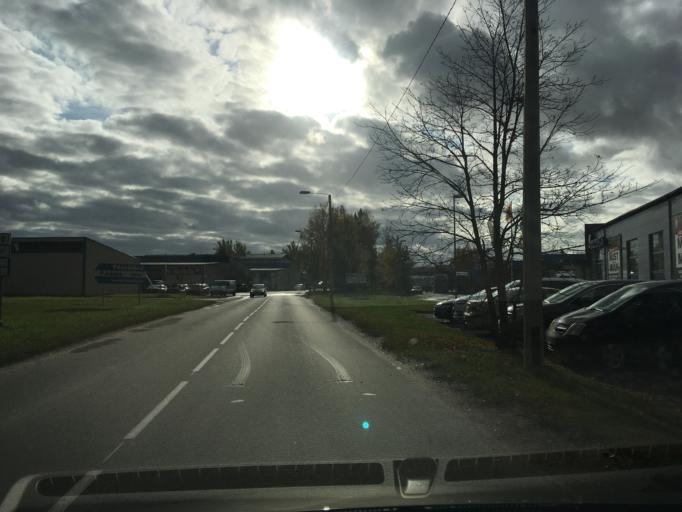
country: EE
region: Paernumaa
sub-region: Paernu linn
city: Parnu
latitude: 58.3746
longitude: 24.5472
